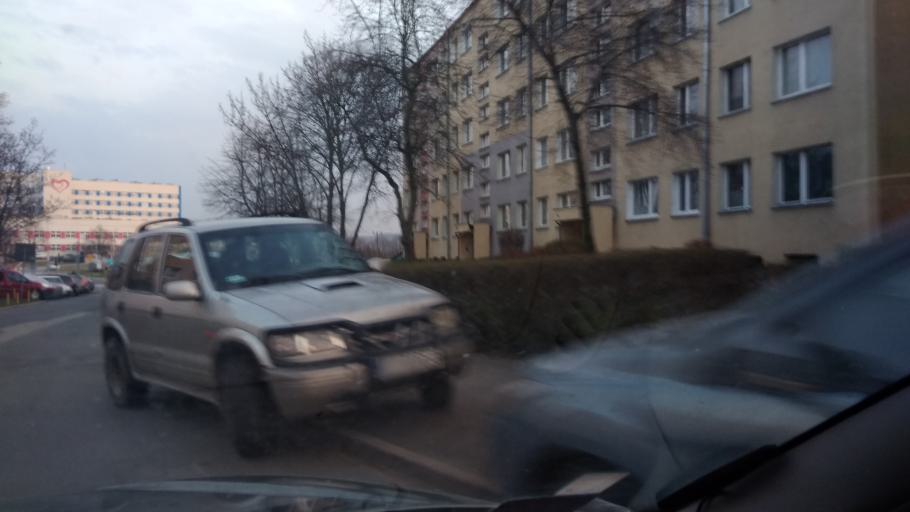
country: PL
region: Lower Silesian Voivodeship
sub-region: Powiat jeleniogorski
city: Jezow Sudecki
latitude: 50.9147
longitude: 15.7612
